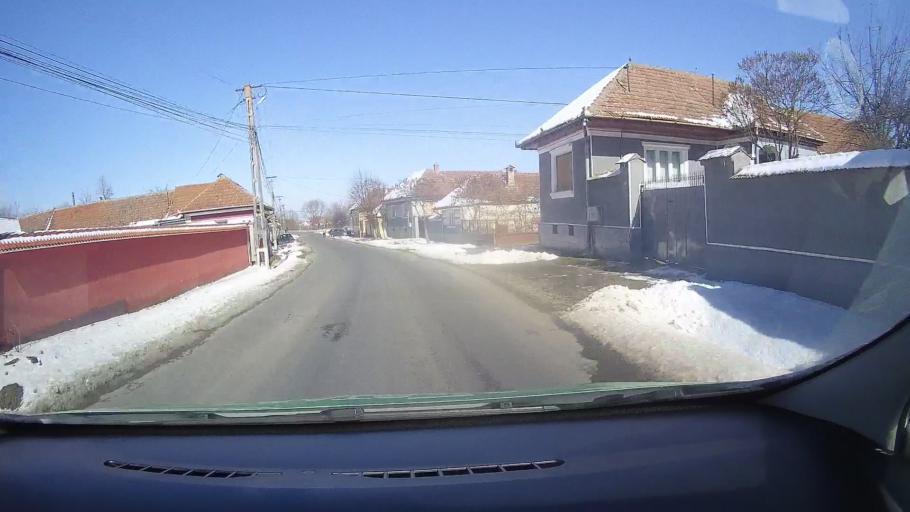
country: RO
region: Brasov
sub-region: Comuna Harseni
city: Harseni
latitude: 45.7863
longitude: 24.9997
